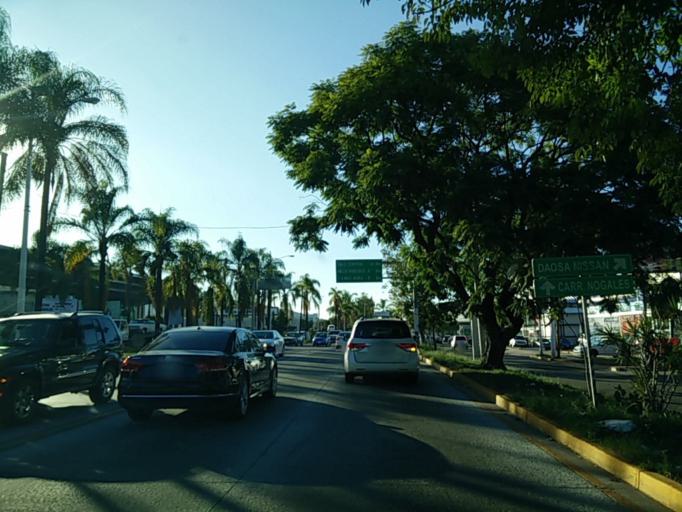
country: MX
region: Jalisco
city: Guadalajara
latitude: 20.6825
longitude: -103.4378
